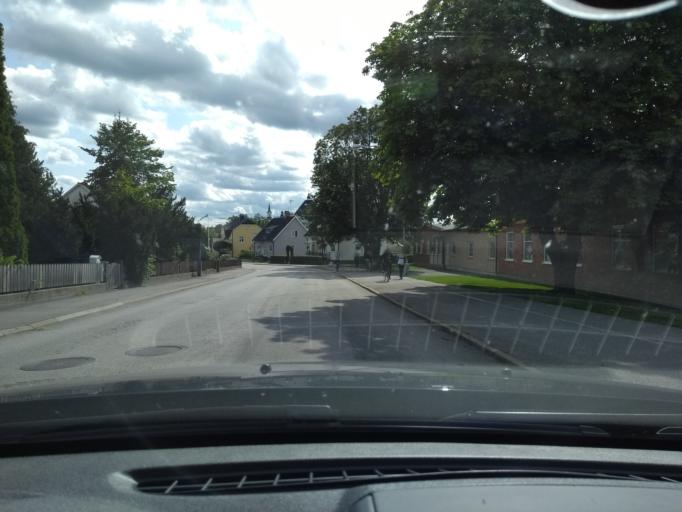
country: SE
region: Kalmar
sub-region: Vimmerby Kommun
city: Vimmerby
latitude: 57.6705
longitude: 15.8573
